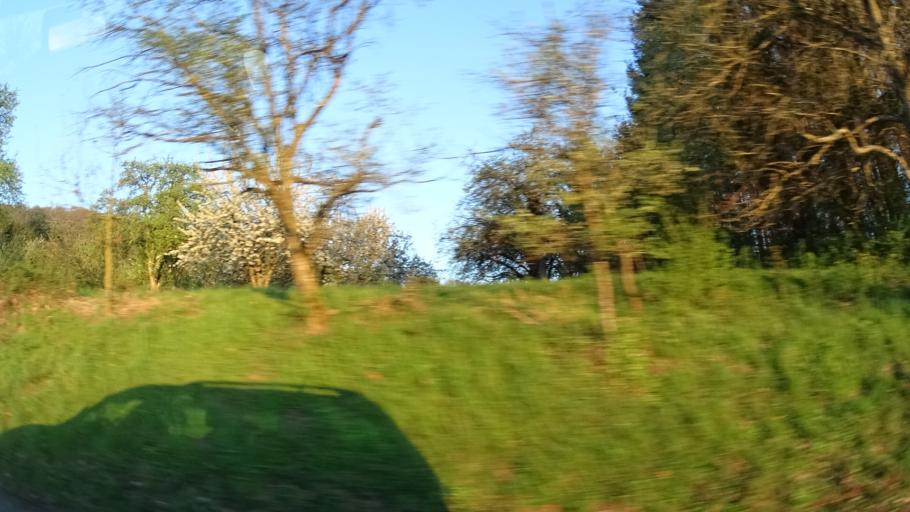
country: DE
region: Baden-Wuerttemberg
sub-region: Regierungsbezirk Stuttgart
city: Pfedelbach
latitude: 49.1683
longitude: 9.4886
